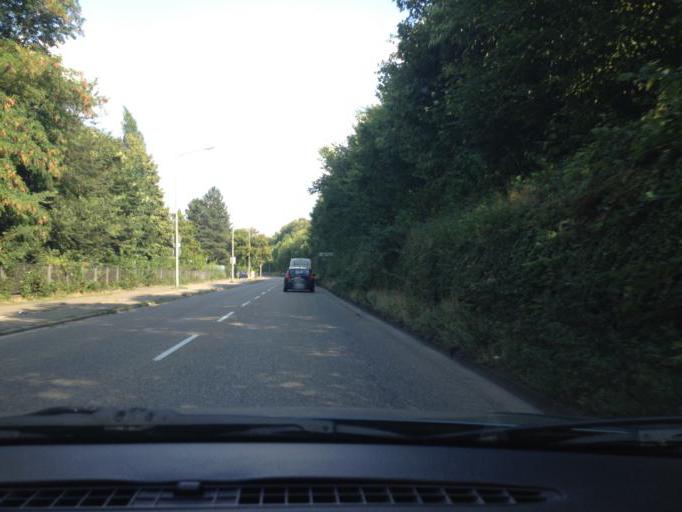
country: DE
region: Rheinland-Pfalz
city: Neustadt
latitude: 49.3515
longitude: 8.1212
